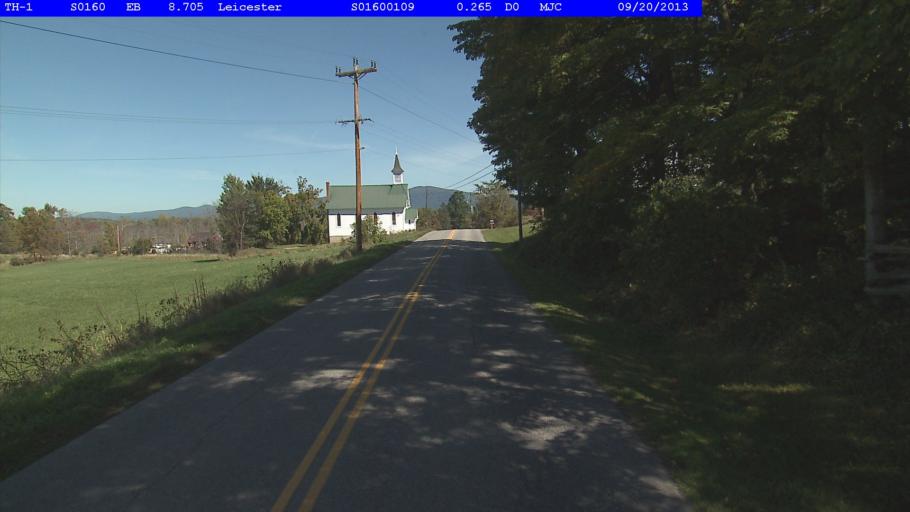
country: US
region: Vermont
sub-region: Rutland County
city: Brandon
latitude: 43.8541
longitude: -73.1537
